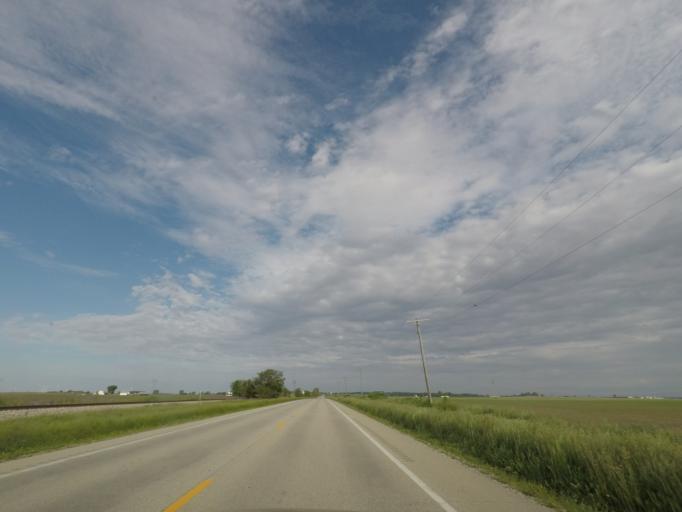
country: US
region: Illinois
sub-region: Logan County
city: Mount Pulaski
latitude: 39.9940
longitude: -89.2512
